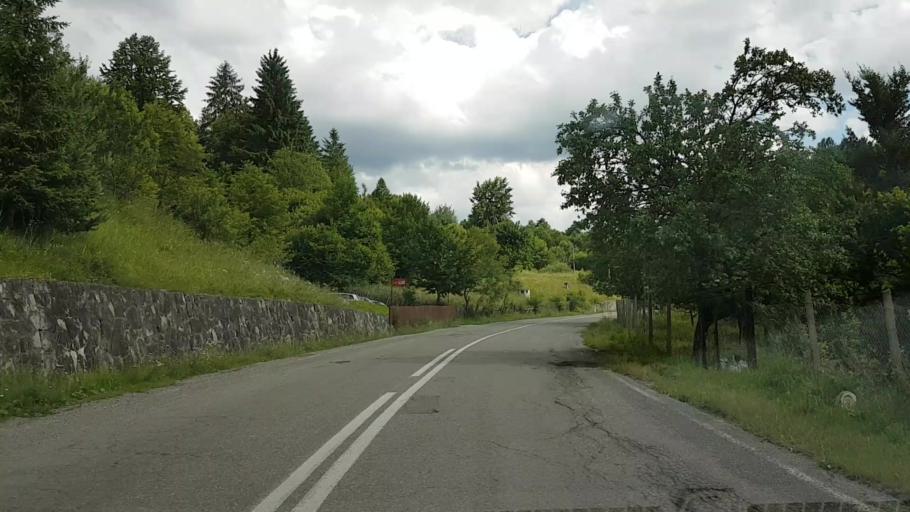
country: RO
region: Neamt
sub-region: Comuna Bicaz
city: Dodeni
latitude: 47.0003
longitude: 26.0983
